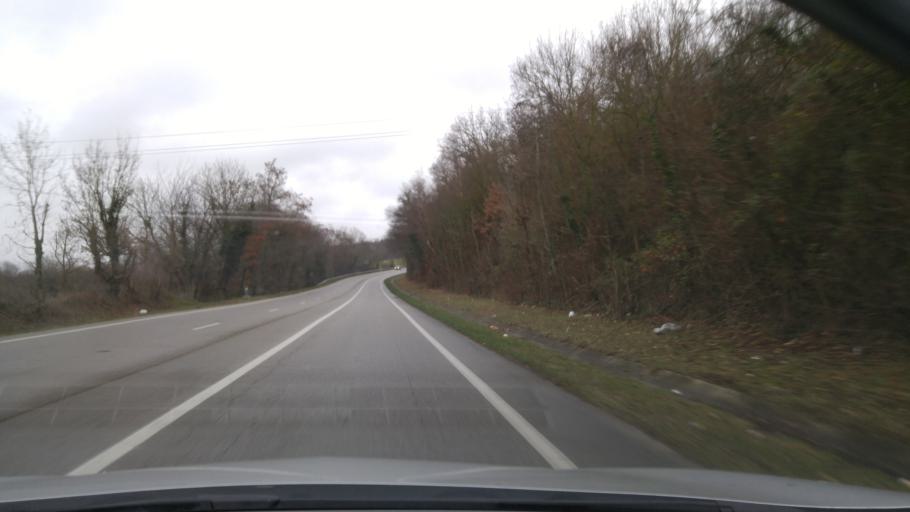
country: FR
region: Rhone-Alpes
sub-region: Departement de l'Isere
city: La Verpilliere
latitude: 45.6299
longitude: 5.1358
